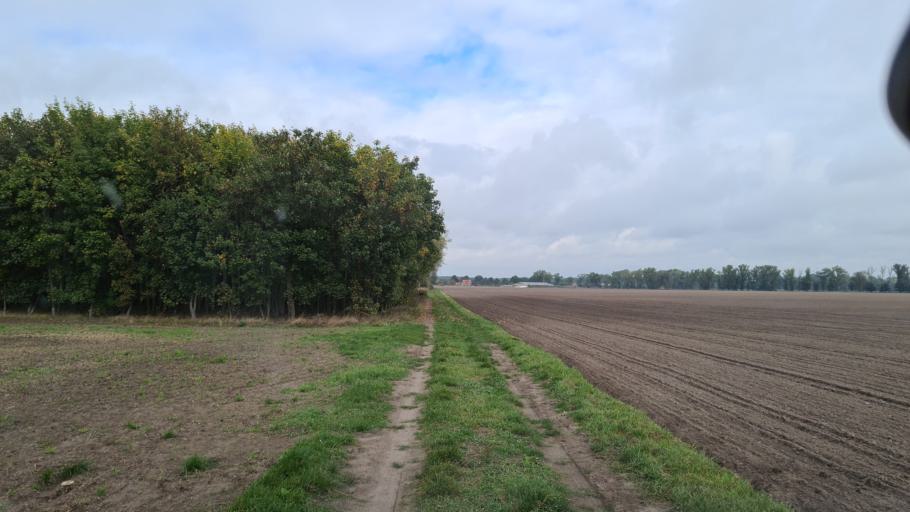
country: DE
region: Brandenburg
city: Schonewalde
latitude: 51.6844
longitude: 13.5697
